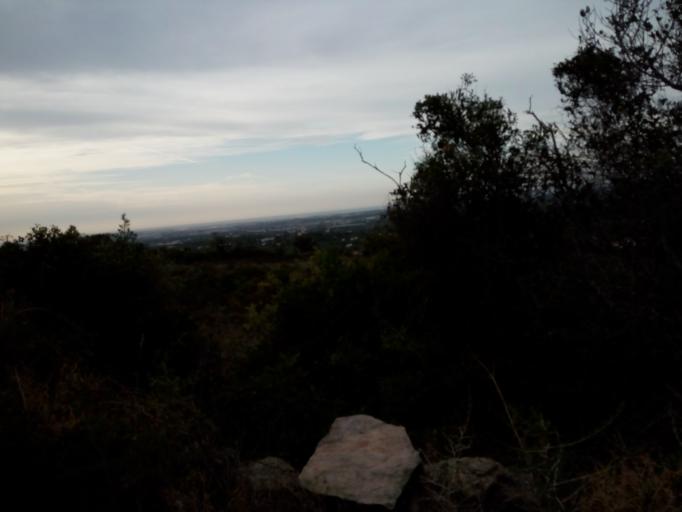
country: PT
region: Faro
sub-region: Faro
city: Santa Barbara de Nexe
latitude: 37.1013
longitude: -7.9574
